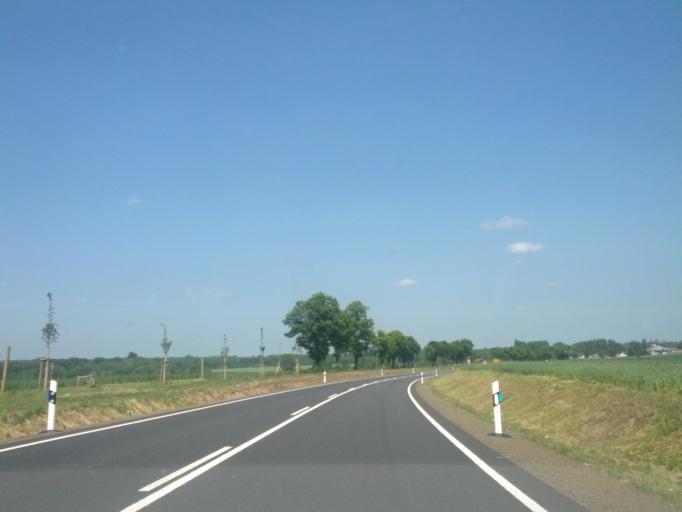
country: DE
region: Thuringia
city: Emleben
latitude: 50.9192
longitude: 10.6535
